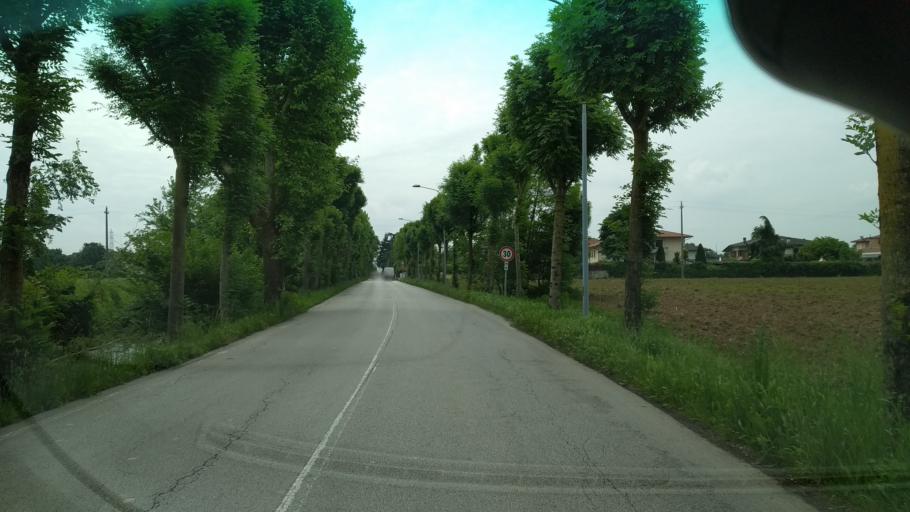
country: IT
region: Veneto
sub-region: Provincia di Vicenza
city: Caldogno-Rettorgole-Cresole
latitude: 45.5973
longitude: 11.5192
